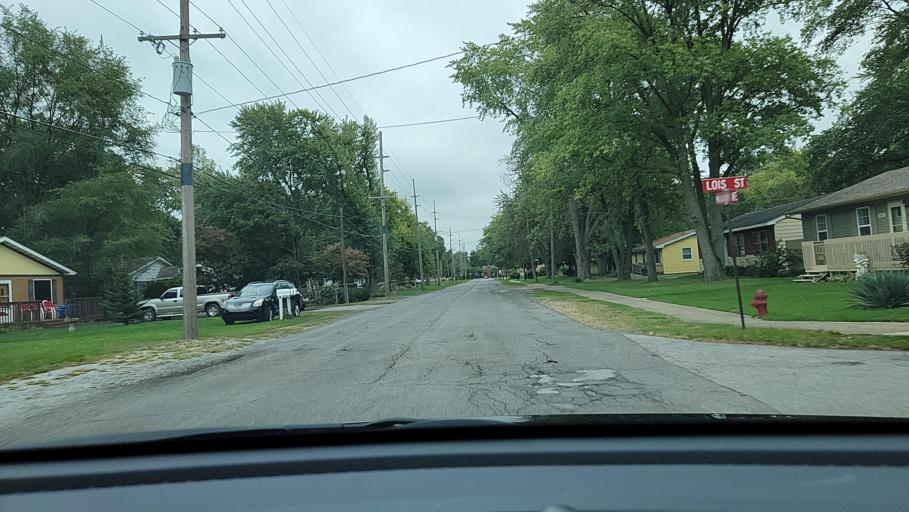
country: US
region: Indiana
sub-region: Porter County
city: Portage
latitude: 41.5717
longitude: -87.1800
